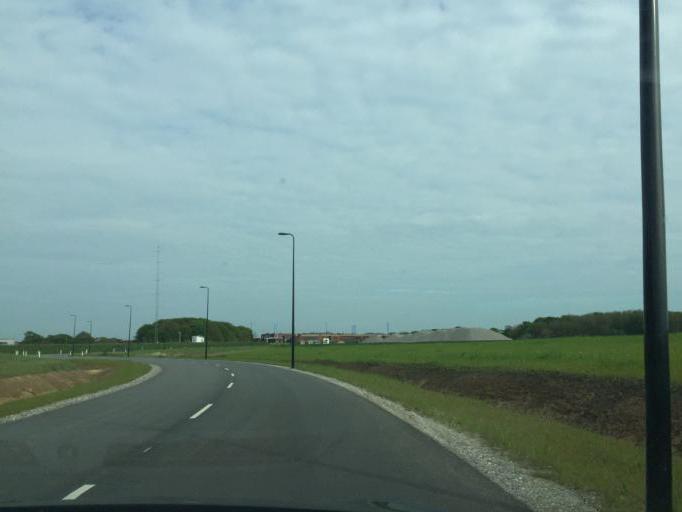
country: DK
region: South Denmark
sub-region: Odense Kommune
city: Neder Holluf
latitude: 55.3704
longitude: 10.4200
